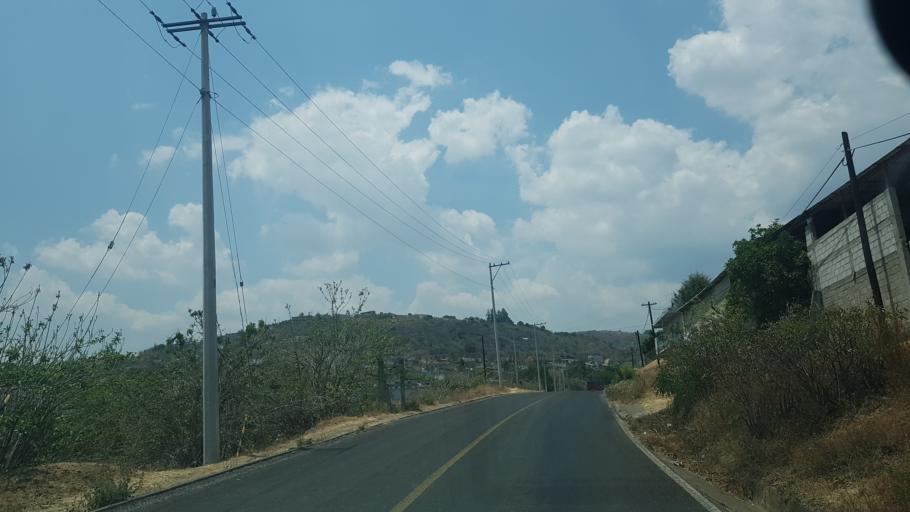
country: MX
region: Puebla
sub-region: Atzitzihuacan
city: Santiago Atzitzihuacan
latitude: 18.8343
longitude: -98.5936
